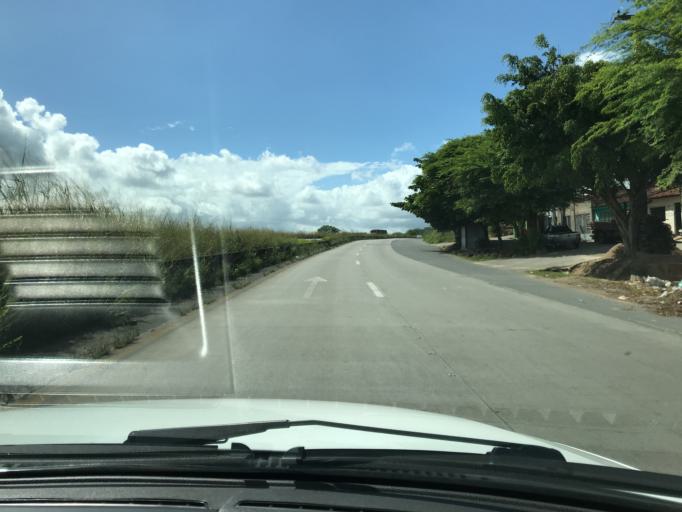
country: BR
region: Pernambuco
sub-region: Pombos
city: Pombos
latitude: -8.1289
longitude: -35.3554
